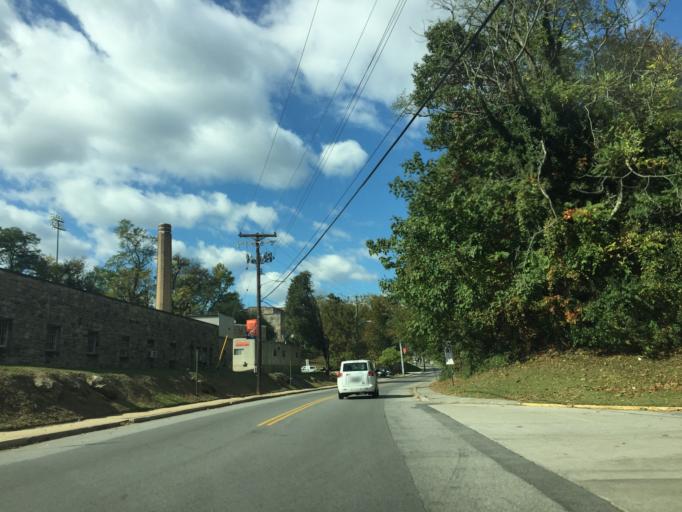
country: US
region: Maryland
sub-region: Baltimore County
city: Parkville
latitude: 39.3453
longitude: -76.5811
